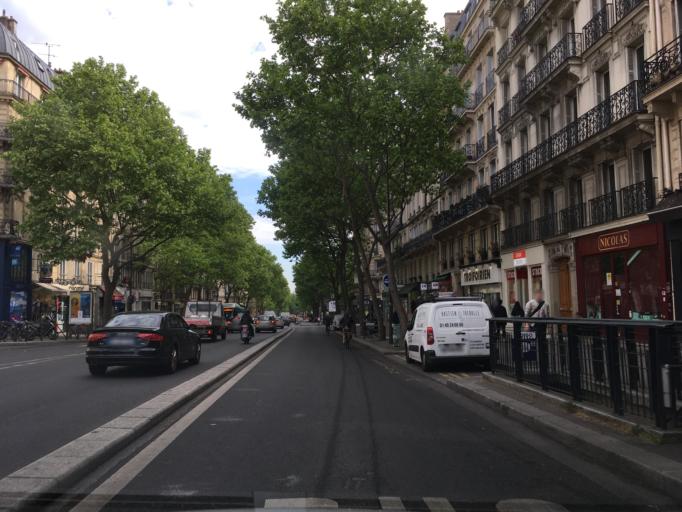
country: FR
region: Ile-de-France
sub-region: Paris
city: Paris
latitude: 48.8476
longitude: 2.3410
